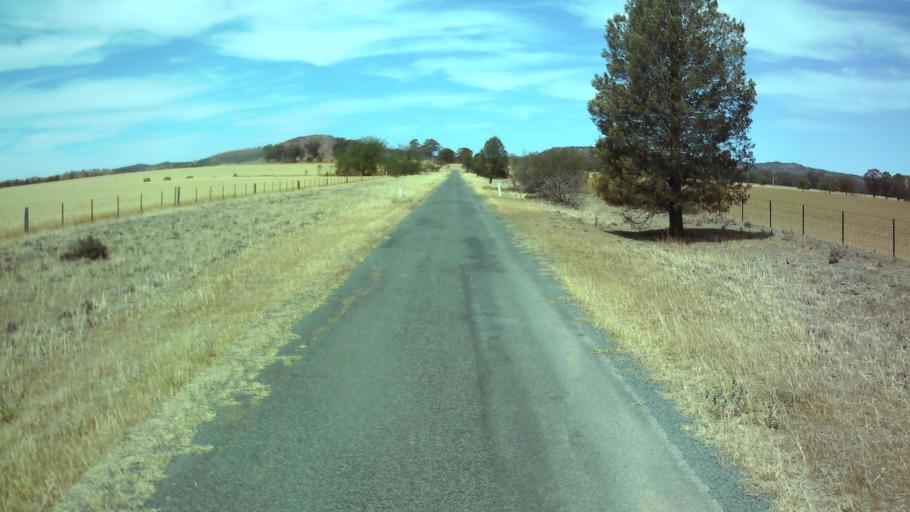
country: AU
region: New South Wales
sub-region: Weddin
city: Grenfell
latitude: -33.7601
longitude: 148.1106
